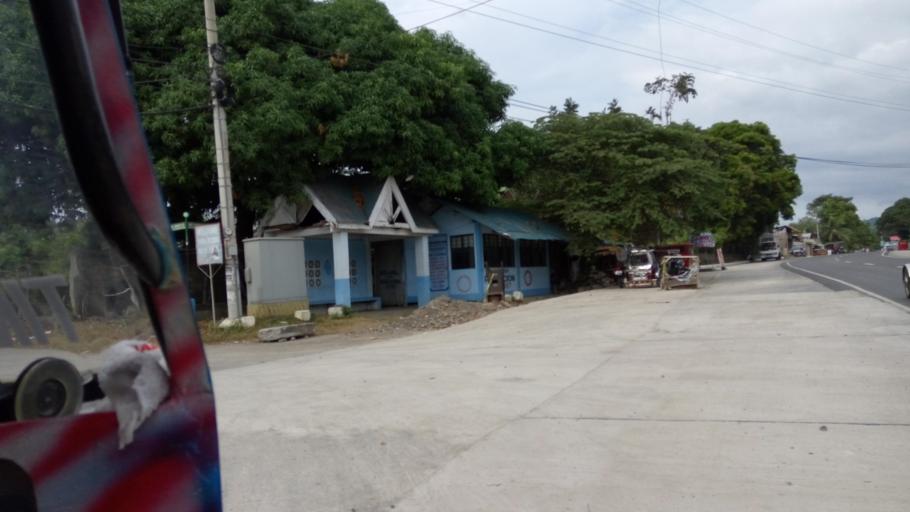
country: PH
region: Ilocos
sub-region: Province of La Union
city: Aringay
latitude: 16.3925
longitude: 120.3564
